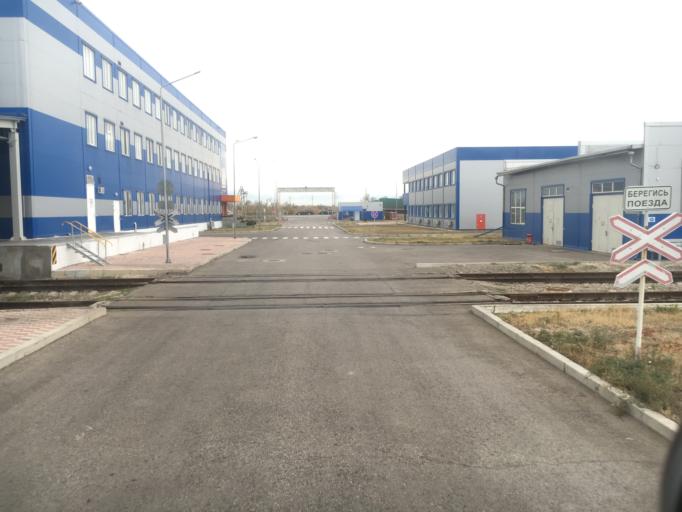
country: KZ
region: Almaty Oblysy
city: Energeticheskiy
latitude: 43.5848
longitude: 77.0931
